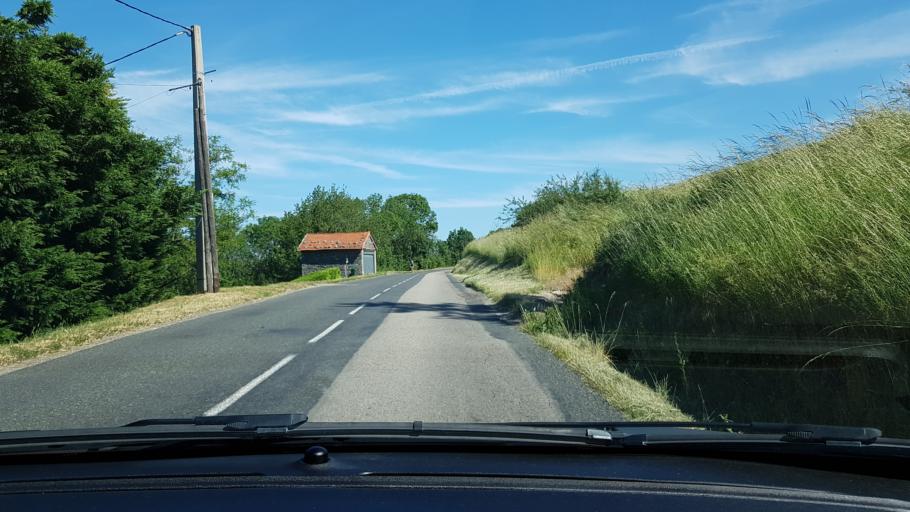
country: FR
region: Rhone-Alpes
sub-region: Departement du Rhone
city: Saint-Maurice-sur-Dargoire
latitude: 45.5893
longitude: 4.6196
